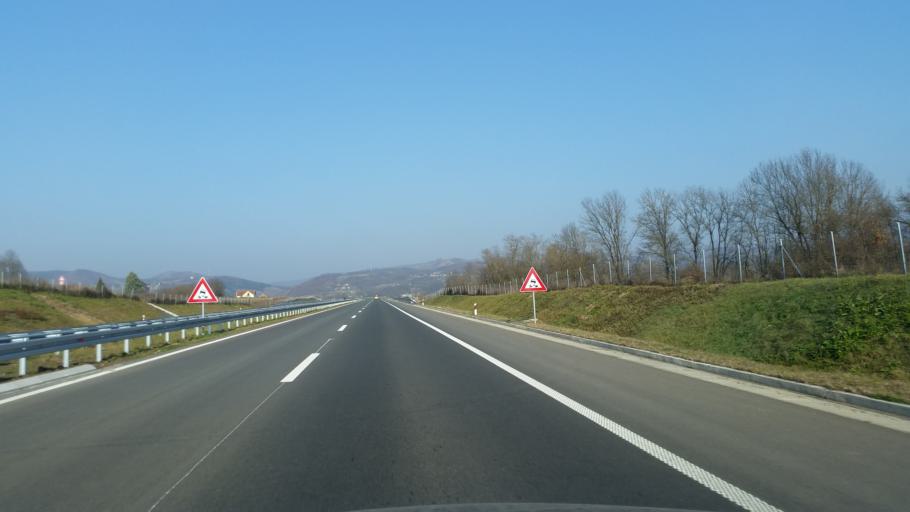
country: RS
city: Prislonica
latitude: 43.9462
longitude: 20.4004
